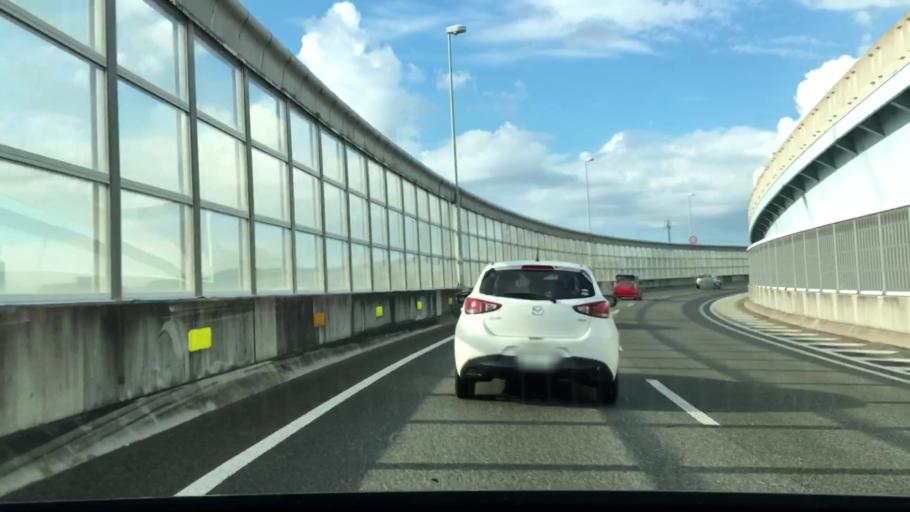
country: JP
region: Fukuoka
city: Fukuoka-shi
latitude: 33.5764
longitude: 130.3158
